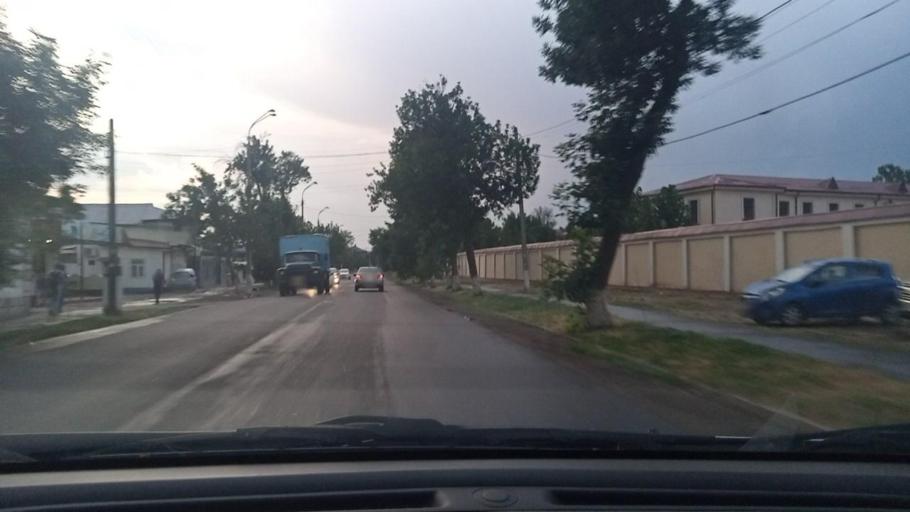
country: UZ
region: Toshkent Shahri
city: Tashkent
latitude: 41.2818
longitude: 69.2853
